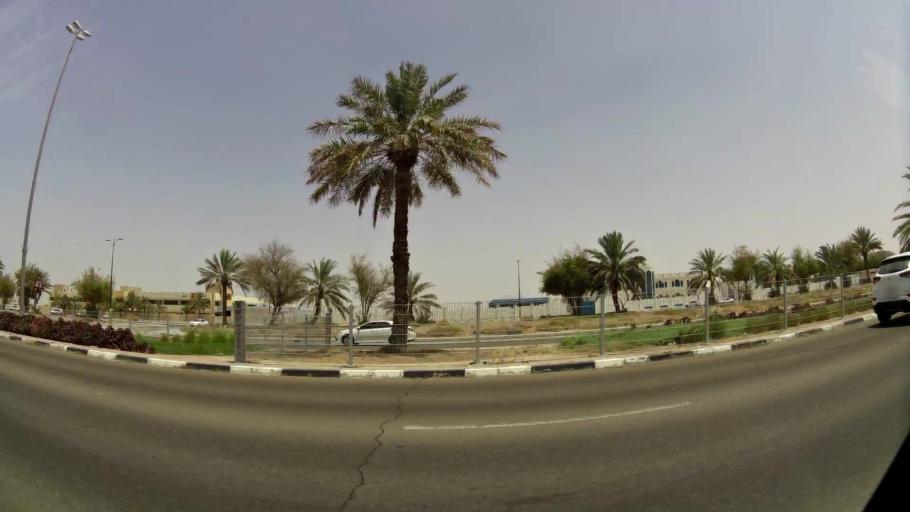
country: AE
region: Abu Dhabi
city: Al Ain
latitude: 24.1995
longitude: 55.7126
